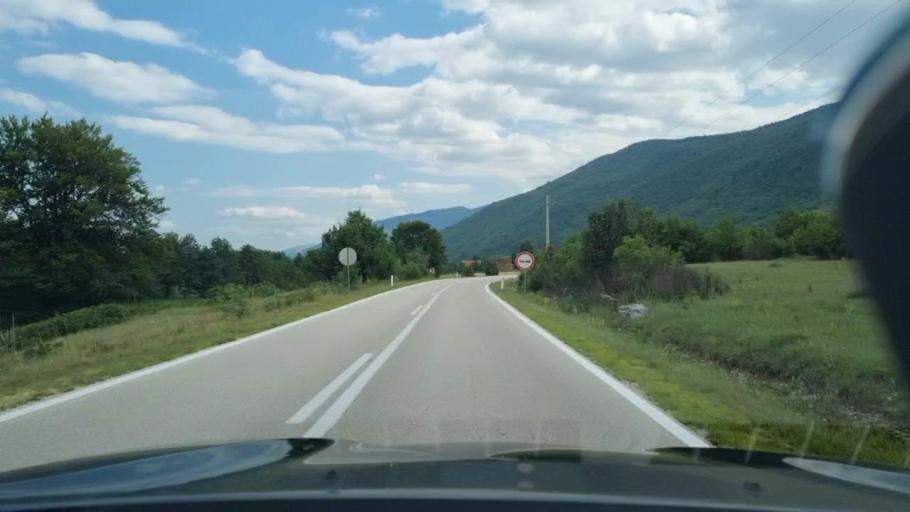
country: BA
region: Federation of Bosnia and Herzegovina
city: Glamoc
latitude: 44.0135
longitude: 16.6029
